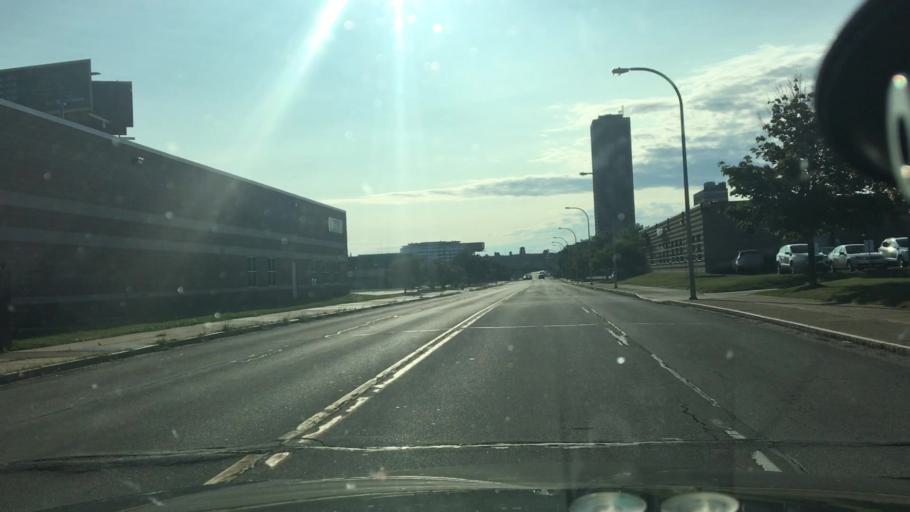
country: US
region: New York
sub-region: Erie County
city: Buffalo
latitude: 42.8771
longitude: -78.8646
